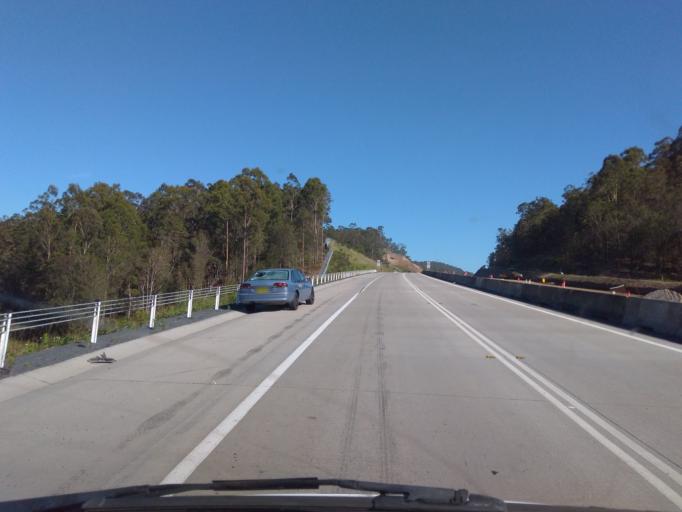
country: AU
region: New South Wales
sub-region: Port Macquarie-Hastings
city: North Shore
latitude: -31.2861
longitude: 152.8160
